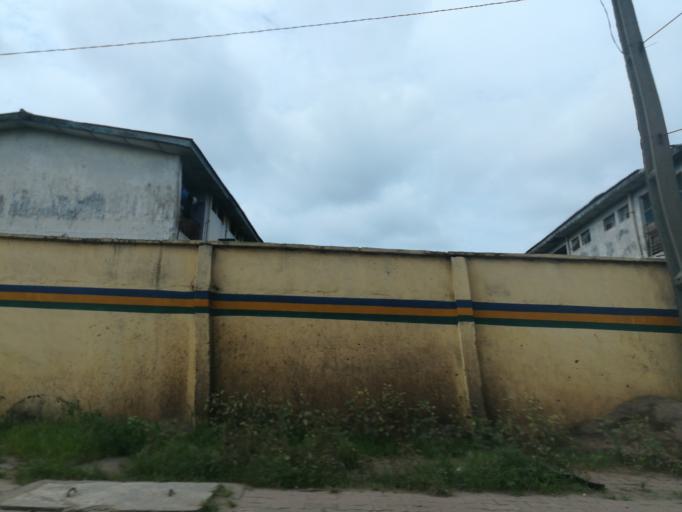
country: NG
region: Lagos
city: Ikeja
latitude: 6.5925
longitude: 3.3467
